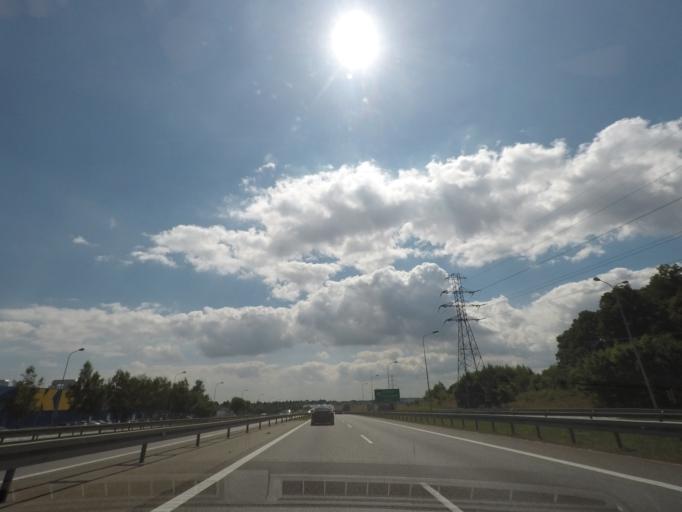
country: PL
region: Pomeranian Voivodeship
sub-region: Powiat gdanski
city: Kowale
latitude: 54.3745
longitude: 18.5146
